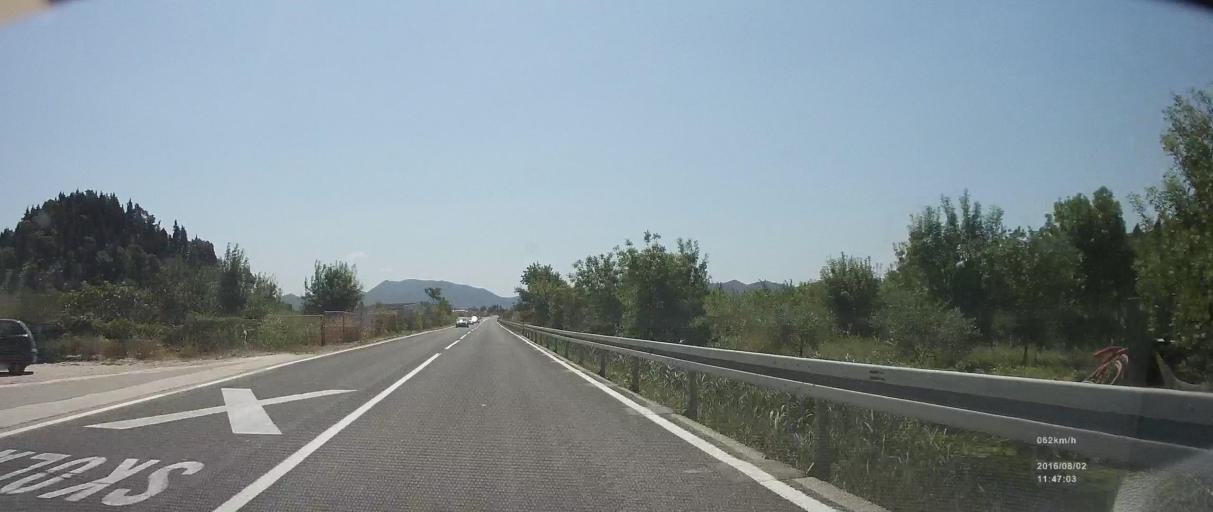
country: HR
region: Dubrovacko-Neretvanska
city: Komin
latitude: 43.0477
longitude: 17.4795
